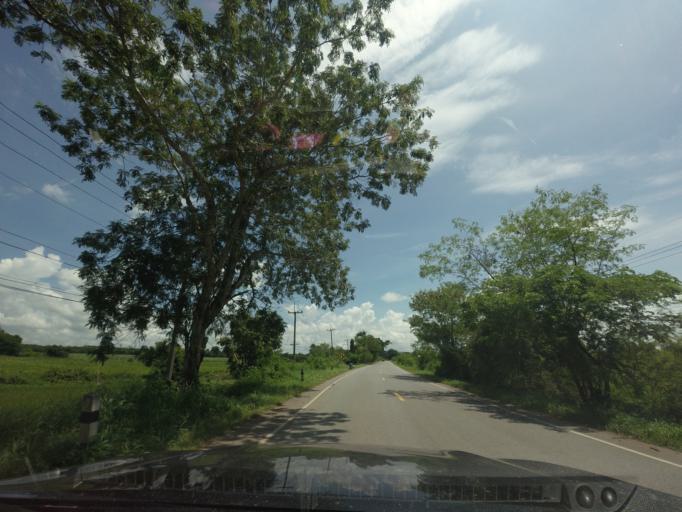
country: TH
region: Changwat Udon Thani
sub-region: Amphoe Ban Phue
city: Ban Phue
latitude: 17.7185
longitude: 102.3964
